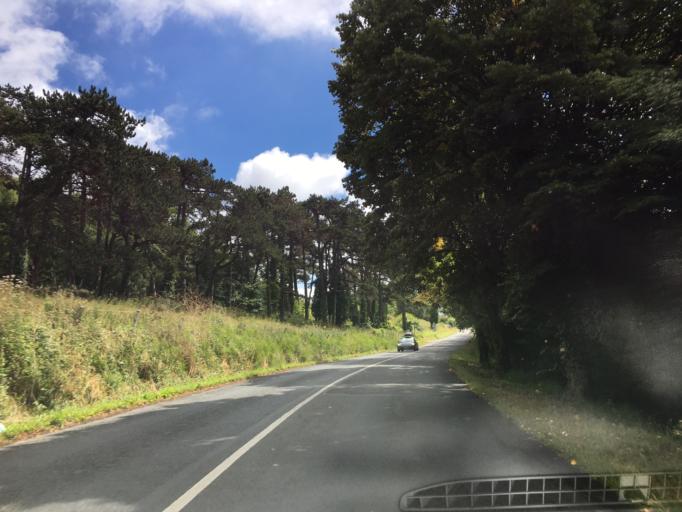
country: FR
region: Lower Normandy
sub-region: Departement du Calvados
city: Houlgate
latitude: 49.2864
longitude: -0.0845
